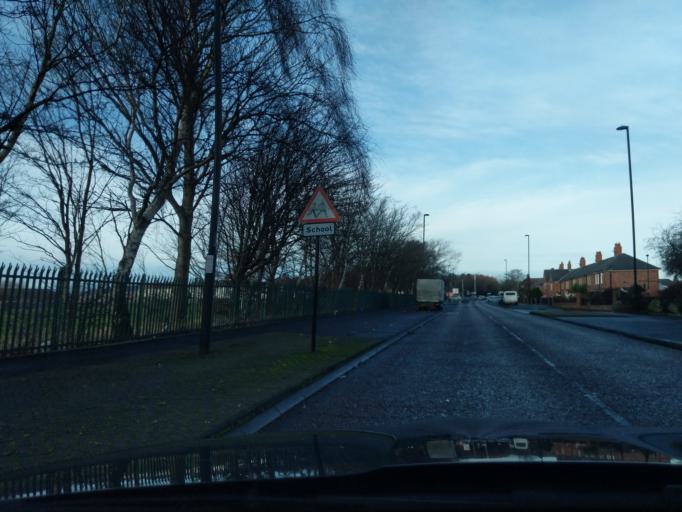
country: GB
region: England
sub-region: Gateshead
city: Felling
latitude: 54.9697
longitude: -1.5683
